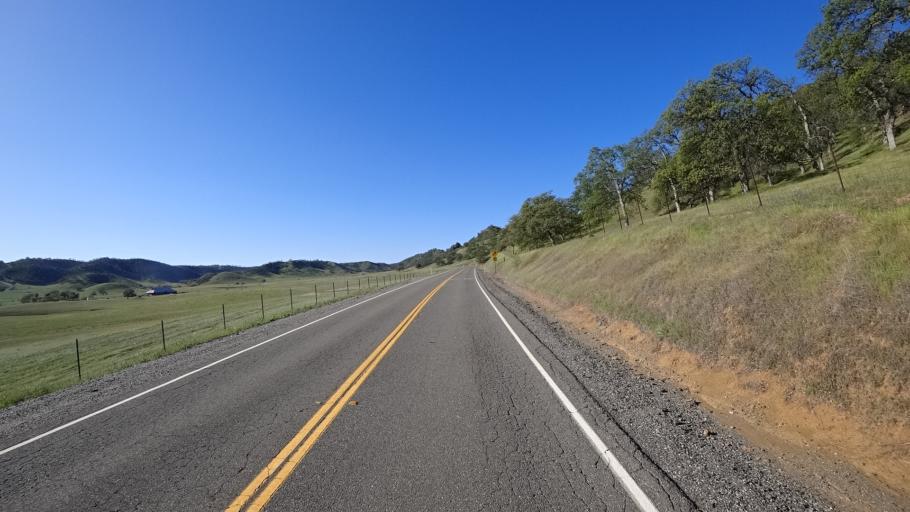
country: US
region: California
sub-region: Tehama County
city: Rancho Tehama Reserve
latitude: 39.7520
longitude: -122.5258
